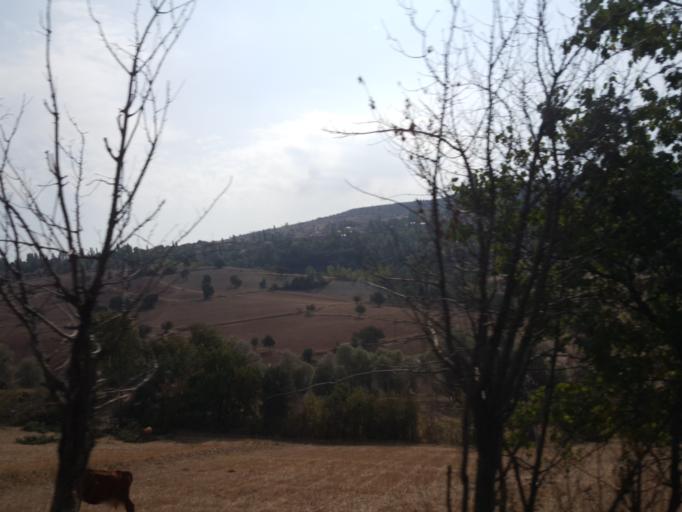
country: TR
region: Tokat
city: Zile
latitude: 40.3688
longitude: 35.8607
